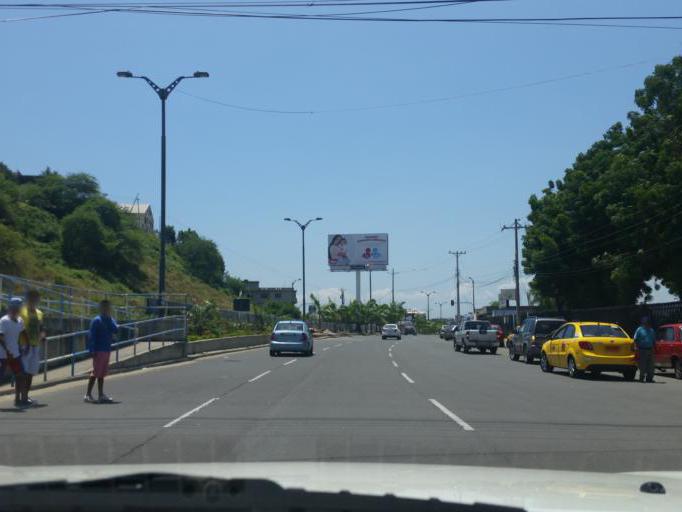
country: EC
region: Manabi
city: Manta
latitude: -0.9542
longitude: -80.7248
